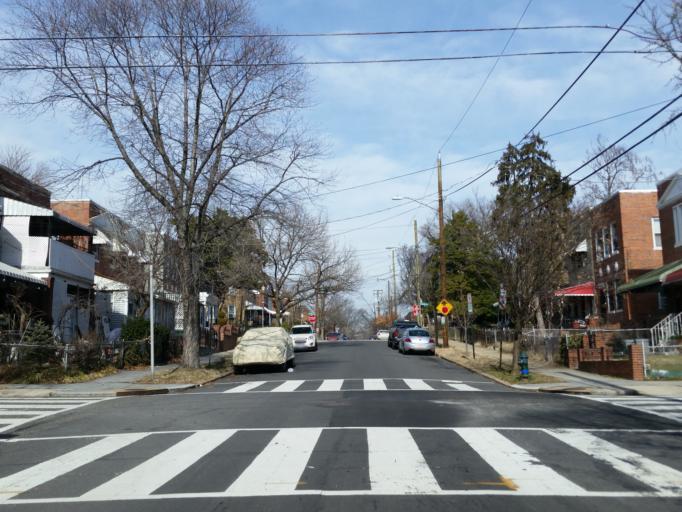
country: US
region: Maryland
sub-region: Montgomery County
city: Takoma Park
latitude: 38.9666
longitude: -77.0225
